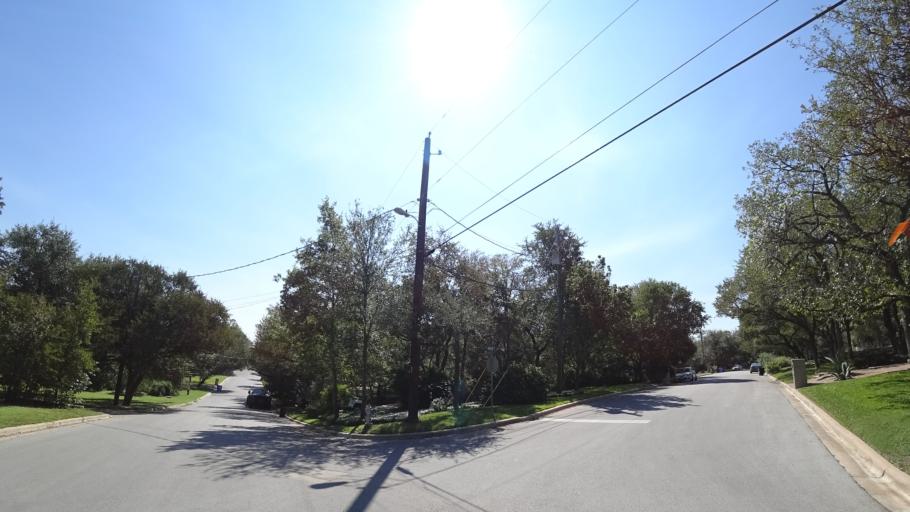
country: US
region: Texas
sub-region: Travis County
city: Rollingwood
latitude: 30.2749
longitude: -97.7811
